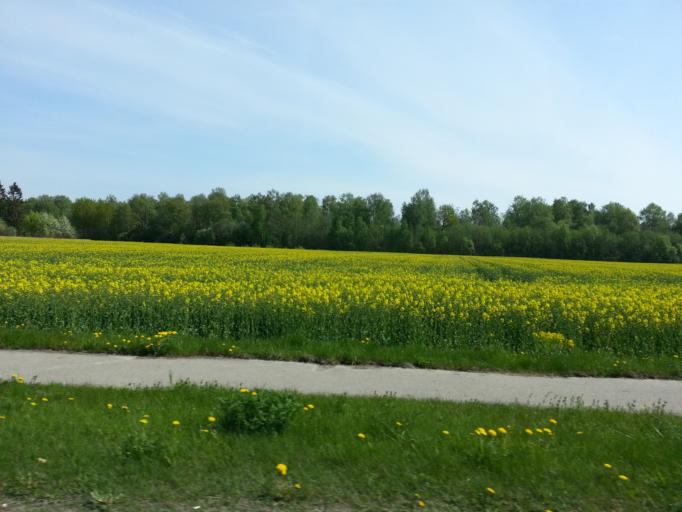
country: LT
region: Panevezys
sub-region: Panevezys City
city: Panevezys
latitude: 55.7723
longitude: 24.2949
